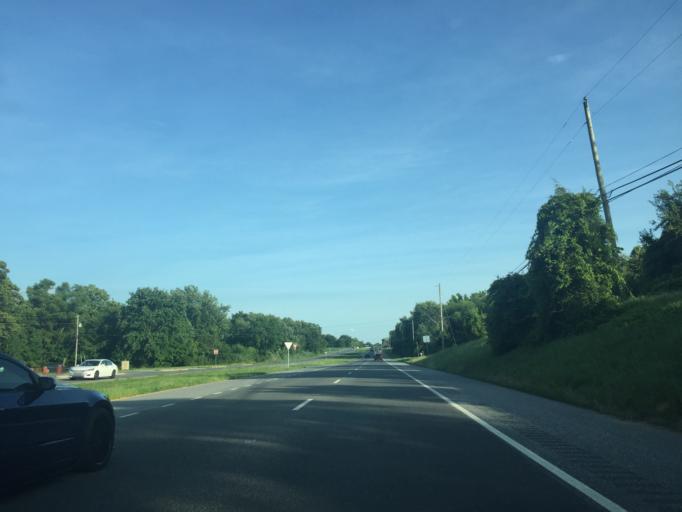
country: US
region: Delaware
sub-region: Kent County
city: Cheswold
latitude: 39.2406
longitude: -75.5862
